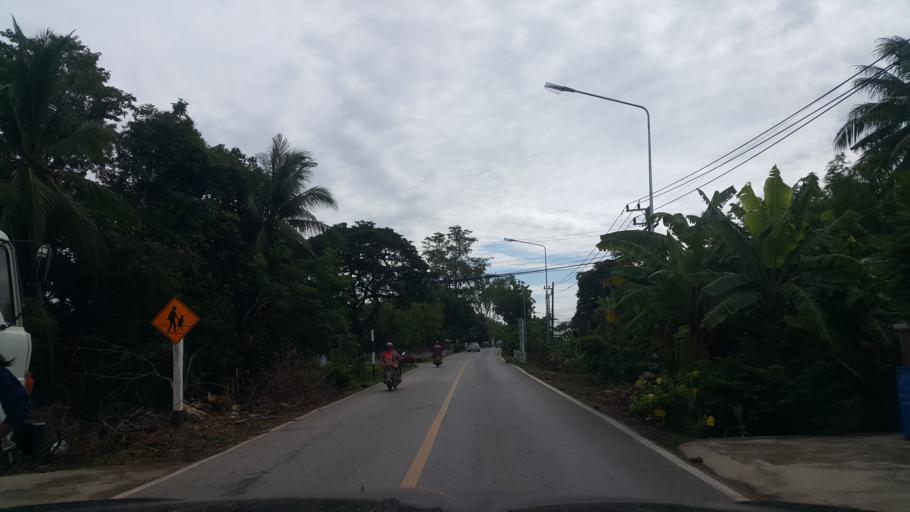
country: TH
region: Uttaradit
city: Phichai
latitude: 17.2918
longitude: 100.0959
